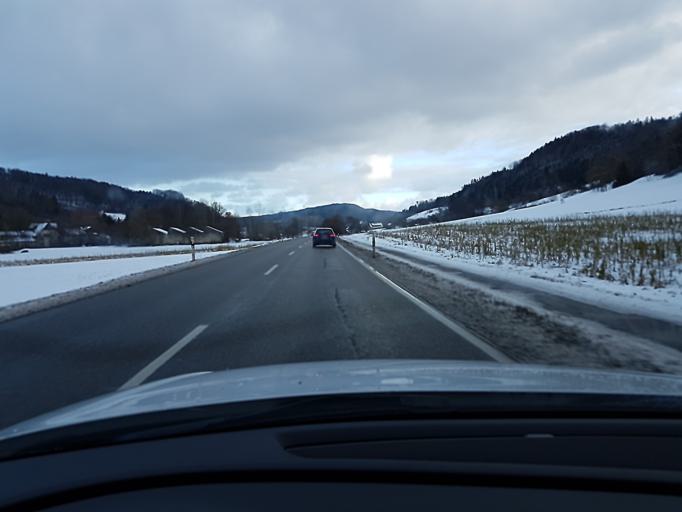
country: DE
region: Baden-Wuerttemberg
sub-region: Regierungsbezirk Stuttgart
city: Murrhardt
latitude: 48.9736
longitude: 9.6080
